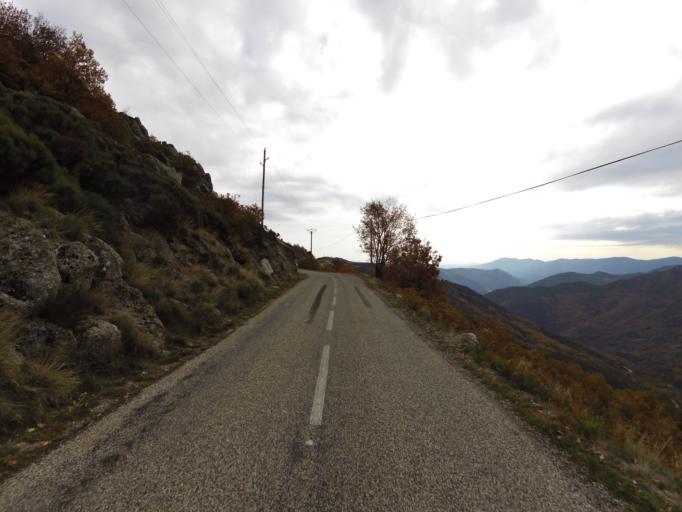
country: FR
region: Rhone-Alpes
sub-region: Departement de l'Ardeche
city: Les Vans
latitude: 44.5116
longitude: 4.0381
